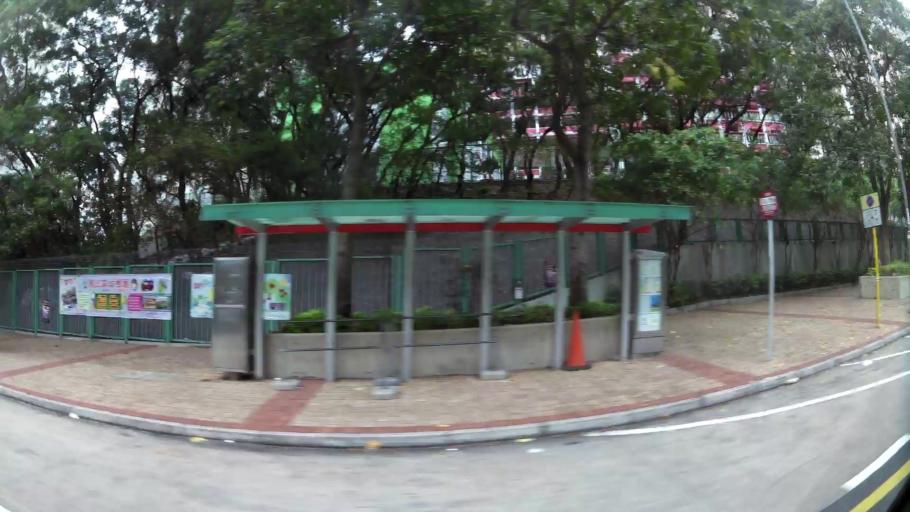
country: HK
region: Kowloon City
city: Kowloon
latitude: 22.3016
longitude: 114.2373
